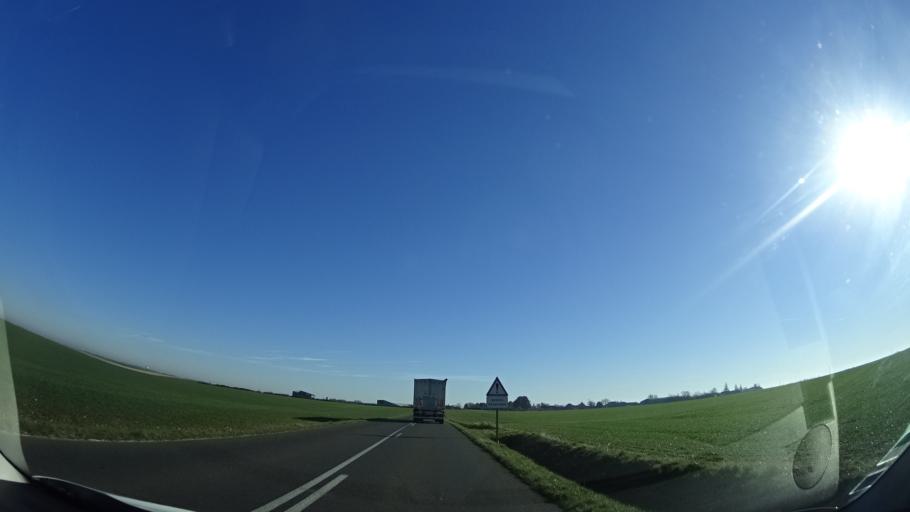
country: FR
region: Poitou-Charentes
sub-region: Departement de la Vienne
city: Moncontour
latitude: 46.8107
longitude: -0.0455
